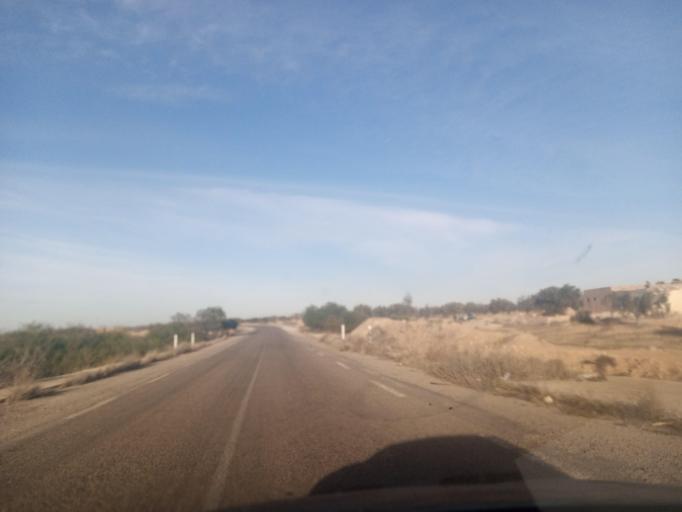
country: TN
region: Al Mahdiyah
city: Shurban
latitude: 34.9494
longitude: 10.3553
